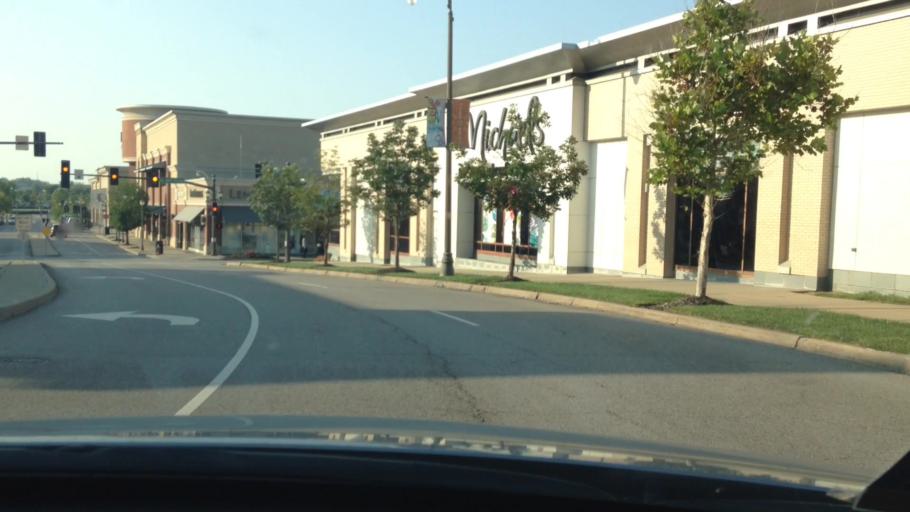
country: US
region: Missouri
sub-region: Platte County
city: Weatherby Lake
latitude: 39.2499
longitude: -94.6611
